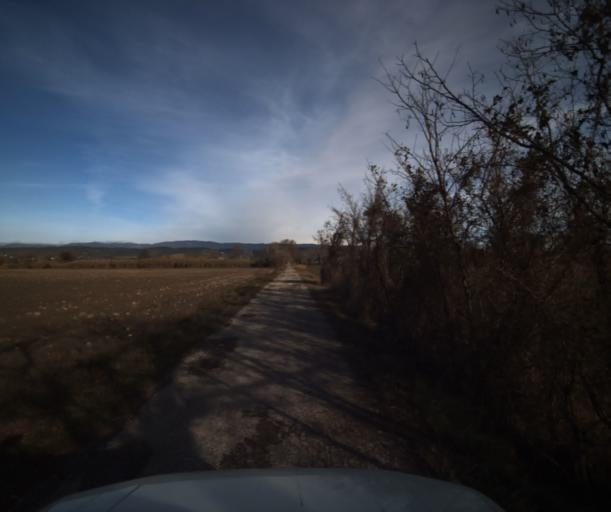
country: FR
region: Provence-Alpes-Cote d'Azur
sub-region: Departement des Bouches-du-Rhone
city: Le Puy-Sainte-Reparade
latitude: 43.6790
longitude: 5.4637
